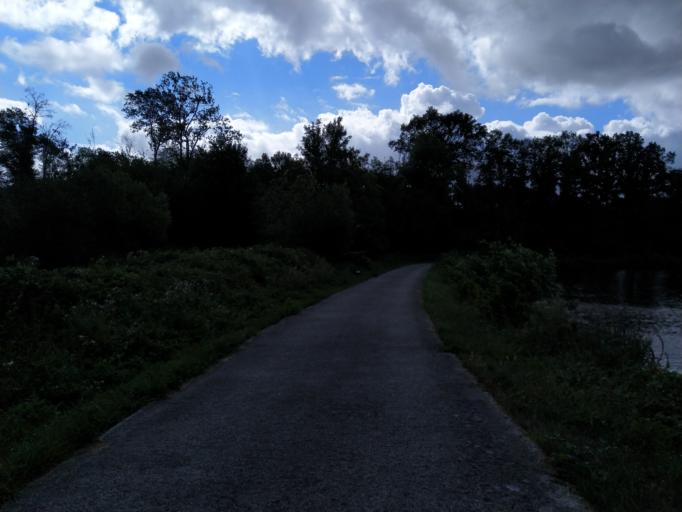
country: BE
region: Wallonia
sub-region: Province du Hainaut
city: Merbes-le-Chateau
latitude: 50.3246
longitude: 4.2178
